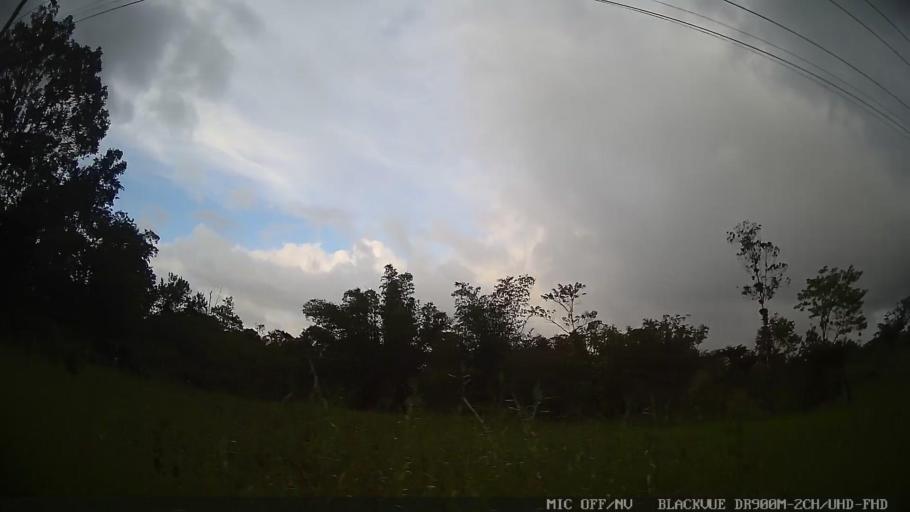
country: BR
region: Sao Paulo
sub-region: Itanhaem
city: Itanhaem
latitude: -24.1051
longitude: -46.8035
